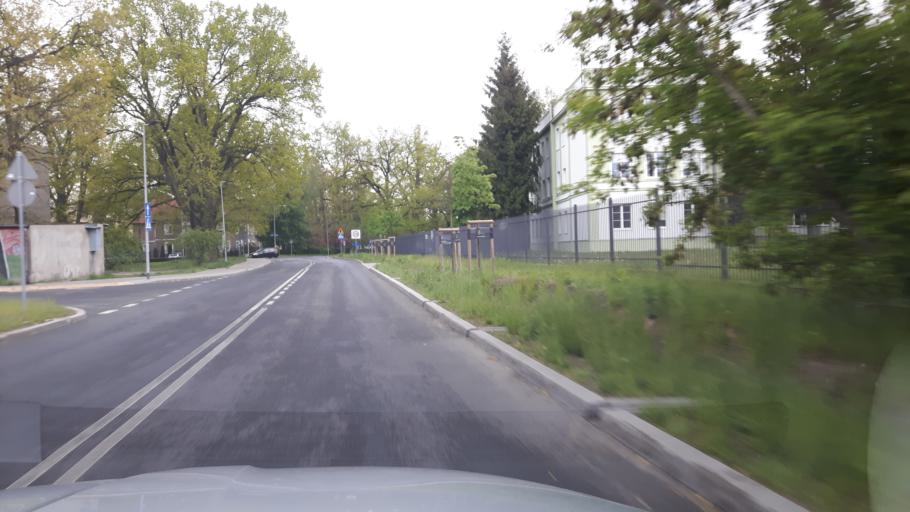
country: PL
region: Masovian Voivodeship
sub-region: Warszawa
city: Rembertow
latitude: 52.2692
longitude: 21.1793
